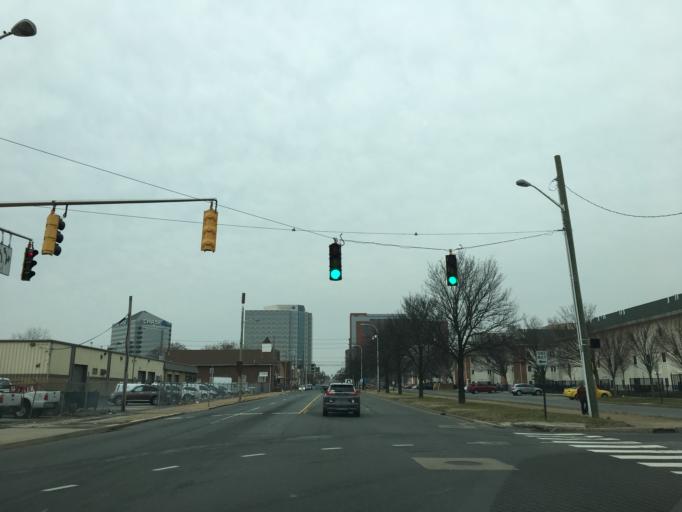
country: US
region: Delaware
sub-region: New Castle County
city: Wilmington
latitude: 39.7374
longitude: -75.5437
